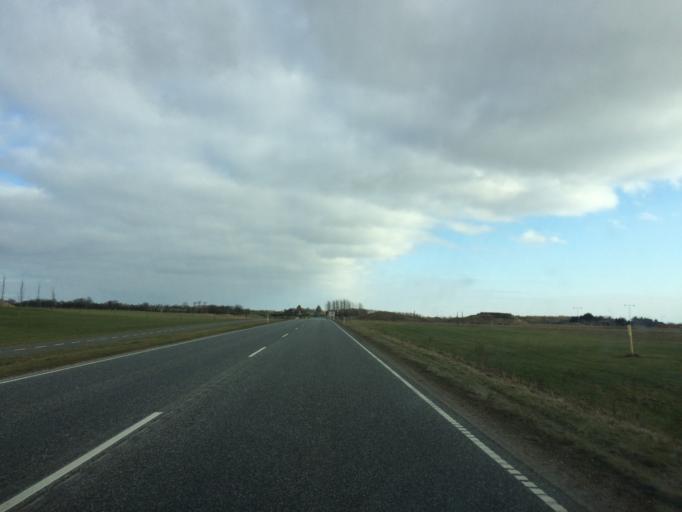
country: DK
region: Central Jutland
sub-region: Holstebro Kommune
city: Holstebro
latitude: 56.3626
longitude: 8.6677
